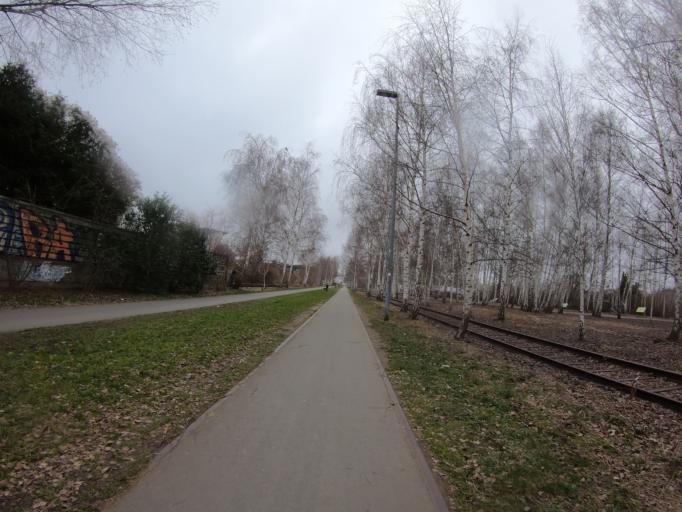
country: DE
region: Lower Saxony
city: Braunschweig
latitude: 52.2517
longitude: 10.5038
